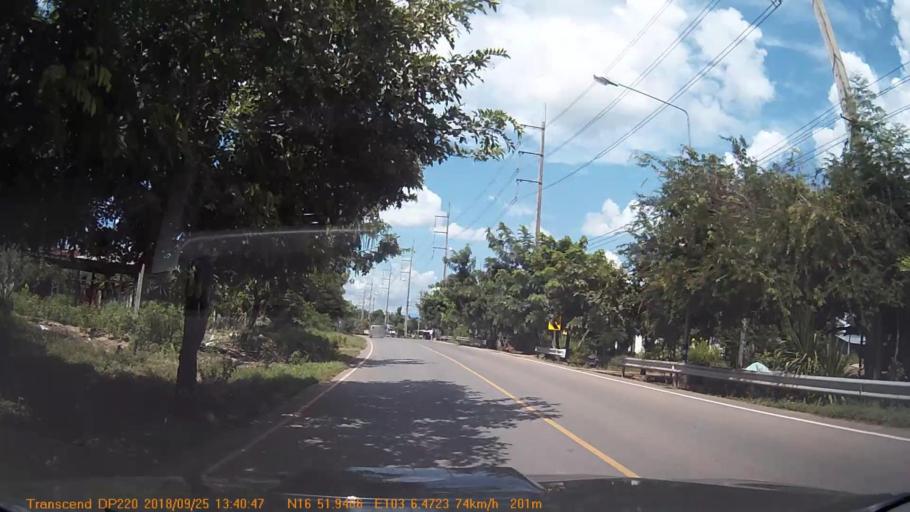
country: TH
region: Changwat Udon Thani
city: Si That
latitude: 16.8658
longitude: 103.1079
